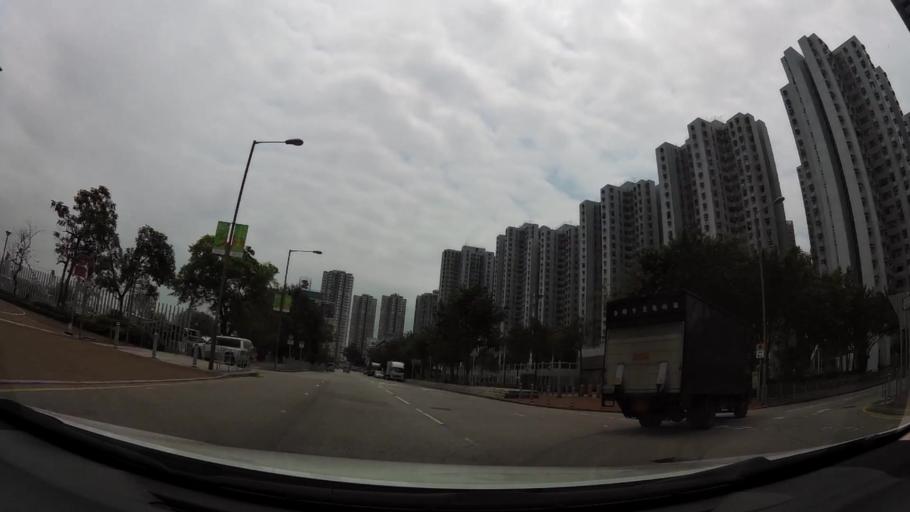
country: HK
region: Tuen Mun
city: Tuen Mun
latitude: 22.3764
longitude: 113.9682
